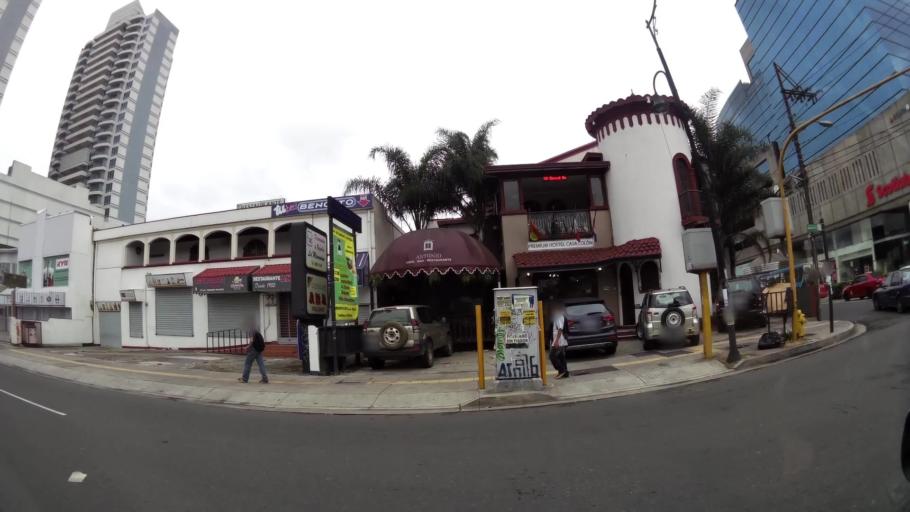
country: CR
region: San Jose
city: San Jose
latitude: 9.9351
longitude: -84.0900
